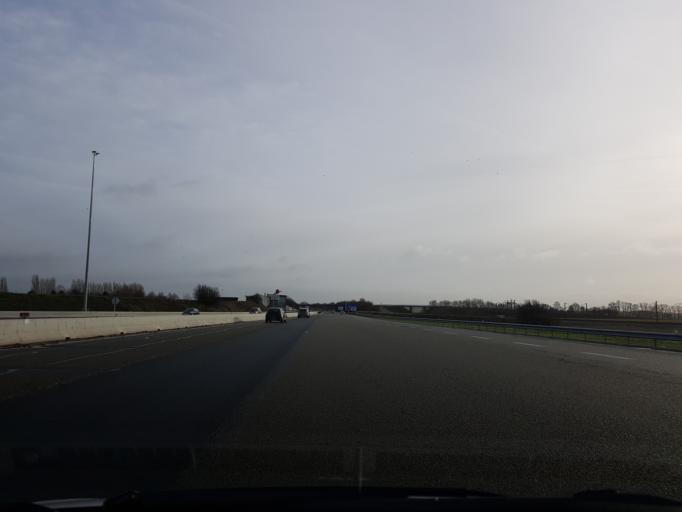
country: FR
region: Ile-de-France
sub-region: Departement de Seine-et-Marne
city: Voisenon
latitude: 48.5884
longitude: 2.6603
